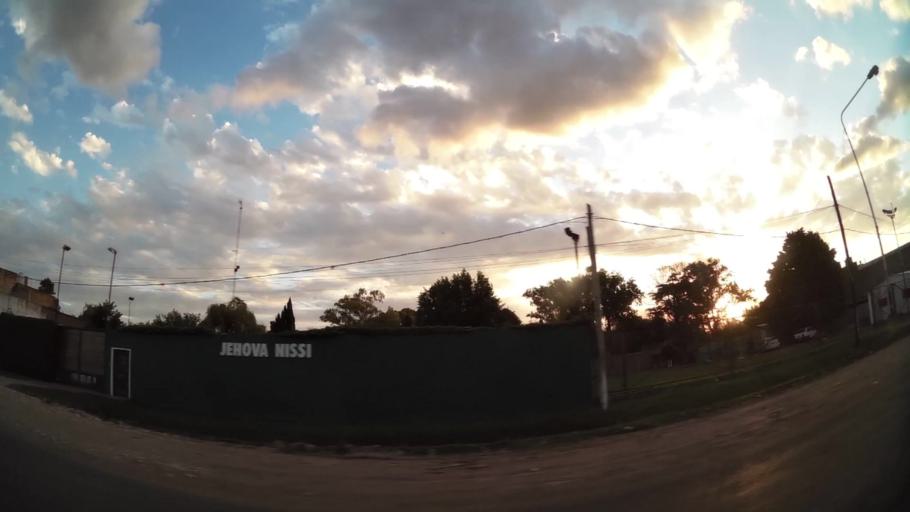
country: AR
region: Buenos Aires
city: Santa Catalina - Dique Lujan
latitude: -34.4905
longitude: -58.7683
